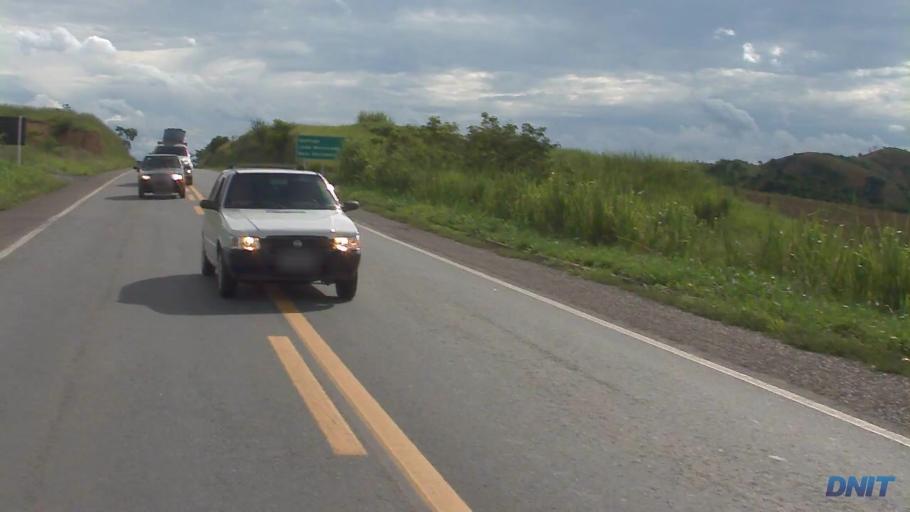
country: BR
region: Minas Gerais
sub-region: Belo Oriente
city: Belo Oriente
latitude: -19.1996
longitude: -42.2869
